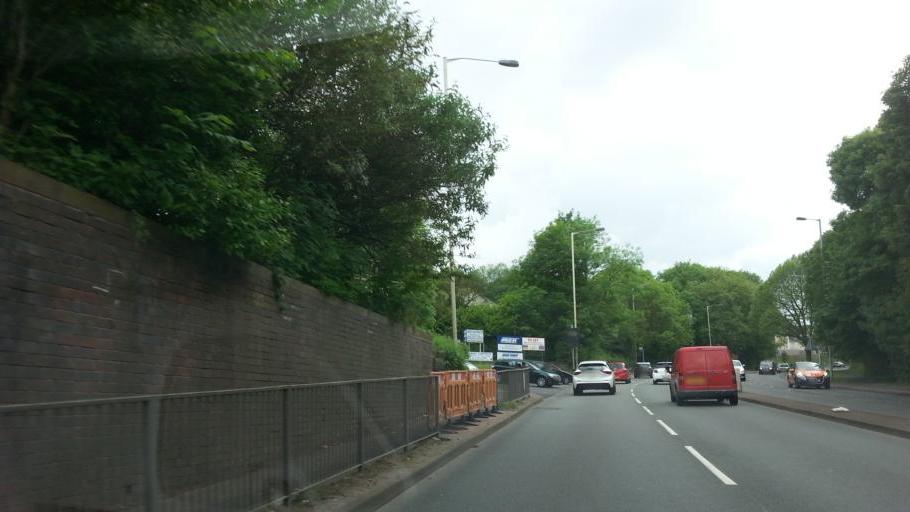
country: GB
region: England
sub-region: Sandwell
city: Tipton
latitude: 52.5241
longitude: -2.0793
